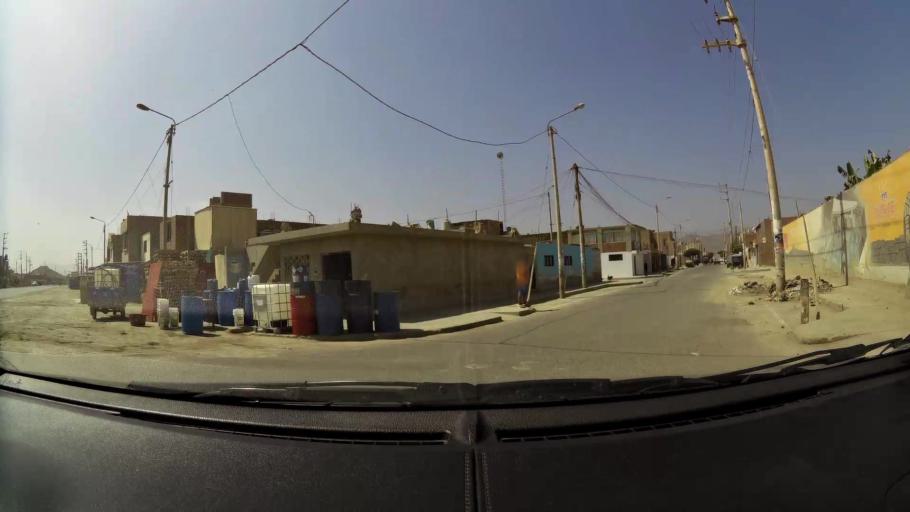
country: PE
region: Ancash
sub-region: Provincia de Huarmey
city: Huarmey
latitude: -10.0690
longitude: -78.1562
